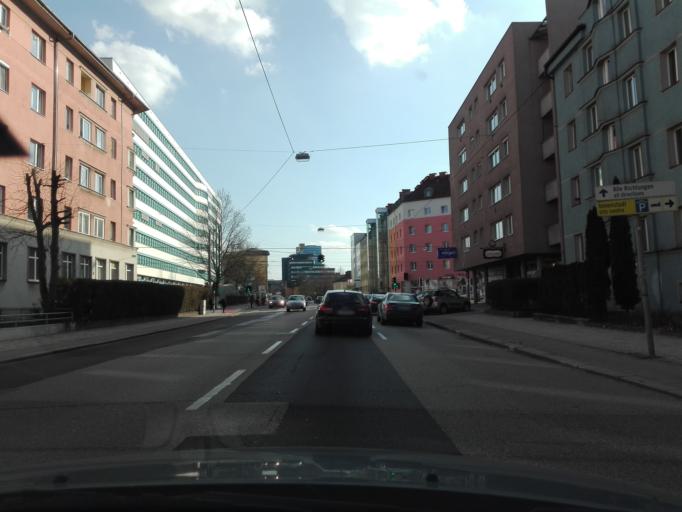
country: AT
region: Upper Austria
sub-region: Linz Stadt
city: Linz
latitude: 48.3041
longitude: 14.3003
